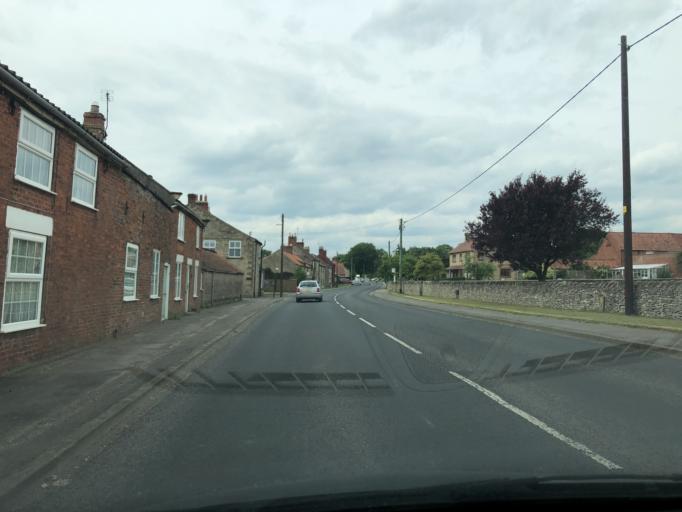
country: GB
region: England
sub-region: North Yorkshire
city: Pickering
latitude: 54.2558
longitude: -0.7968
